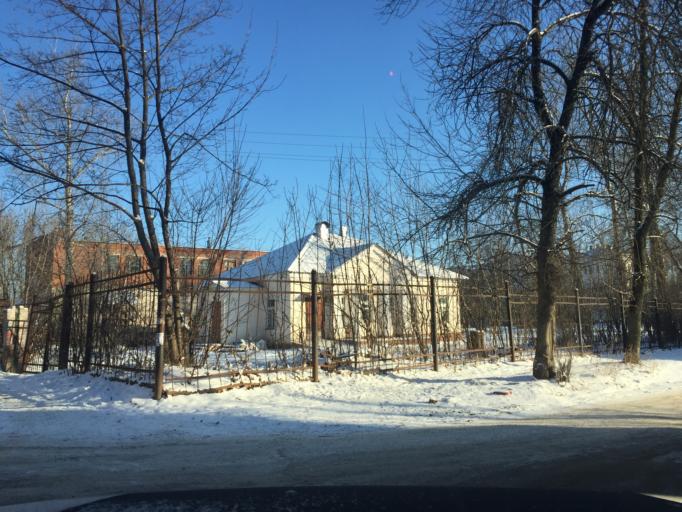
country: RU
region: Tula
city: Tula
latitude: 54.1874
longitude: 37.6965
